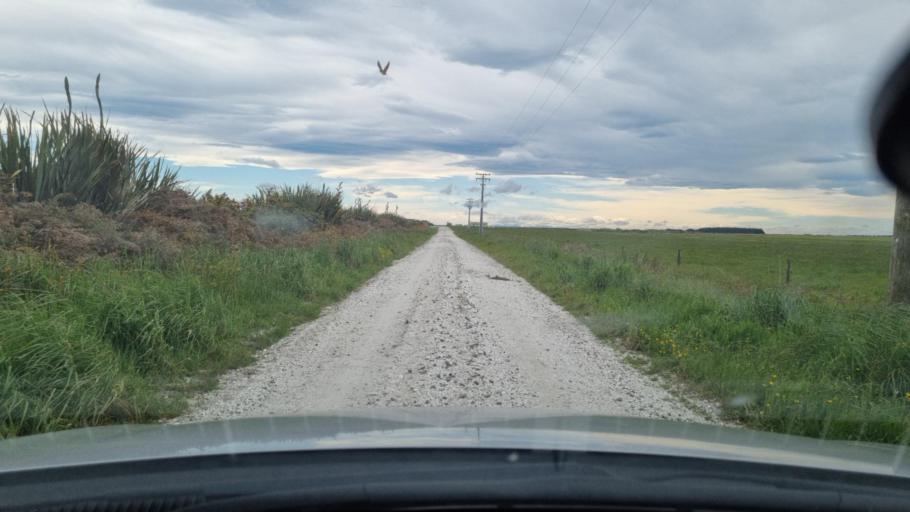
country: NZ
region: Southland
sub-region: Invercargill City
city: Bluff
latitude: -46.5310
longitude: 168.3838
